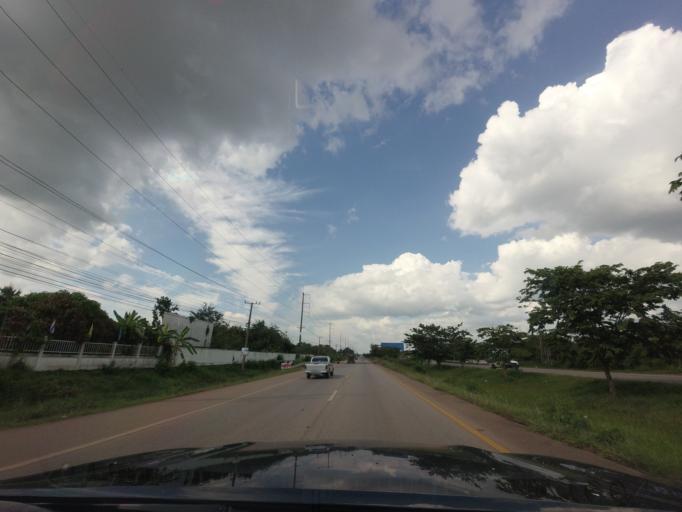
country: TH
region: Changwat Udon Thani
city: Udon Thani
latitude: 17.5147
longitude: 102.7987
